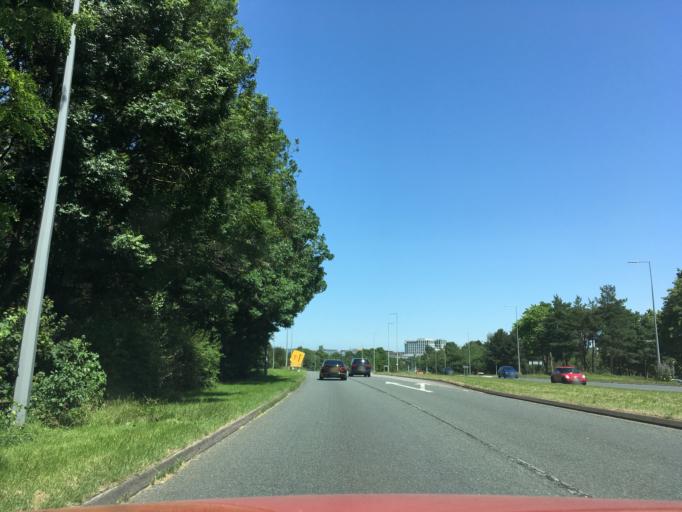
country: GB
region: England
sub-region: Milton Keynes
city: Loughton
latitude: 52.0246
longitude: -0.7760
